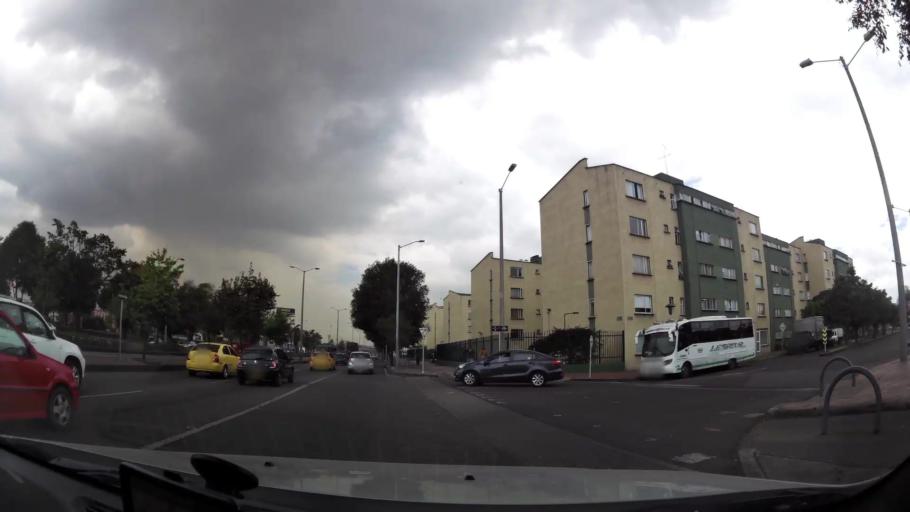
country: CO
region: Bogota D.C.
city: Barrio San Luis
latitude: 4.6804
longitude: -74.0761
